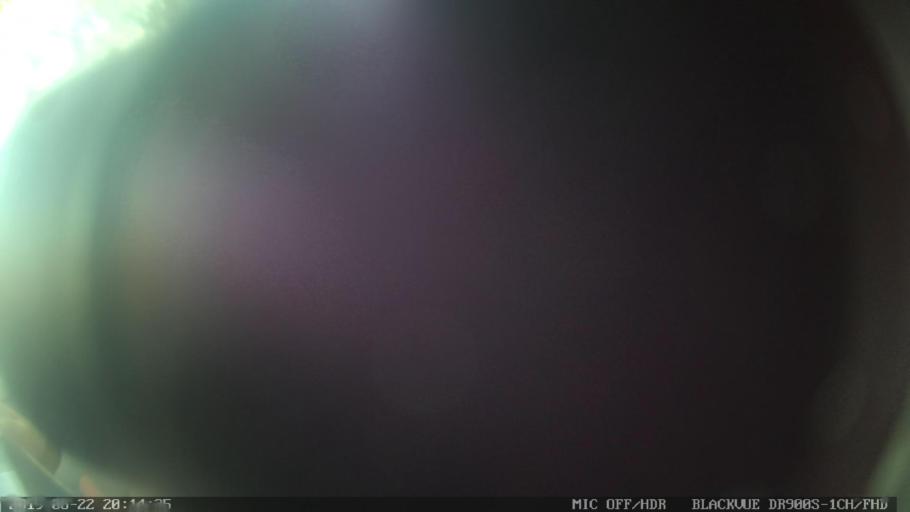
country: PT
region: Guarda
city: Alcains
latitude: 39.9217
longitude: -7.4296
